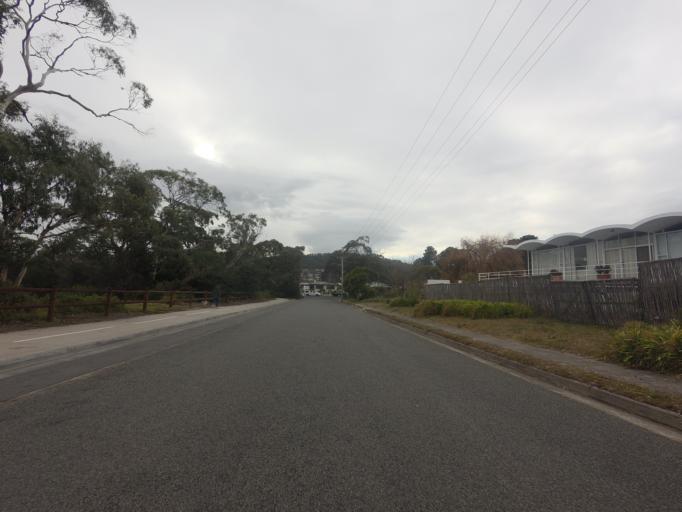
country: AU
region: Tasmania
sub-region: Clarence
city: Bellerive
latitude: -42.8803
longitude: 147.3850
